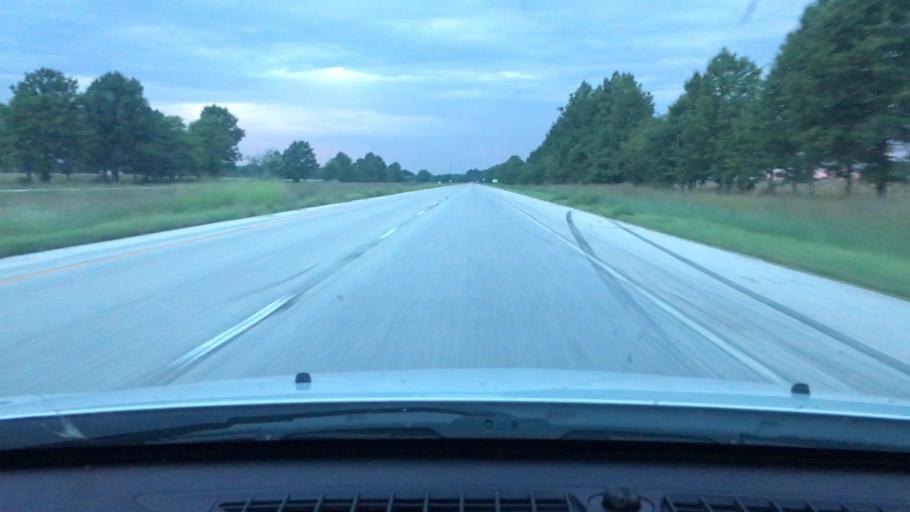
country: US
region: Illinois
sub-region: Morgan County
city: Jacksonville
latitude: 39.7380
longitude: -90.1325
